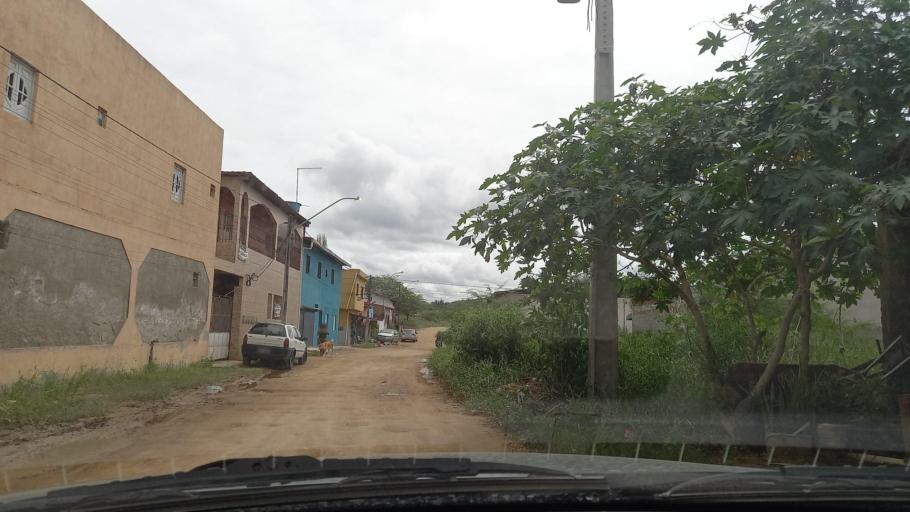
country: ET
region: Oromiya
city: Gore
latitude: 8.1934
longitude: 35.5800
